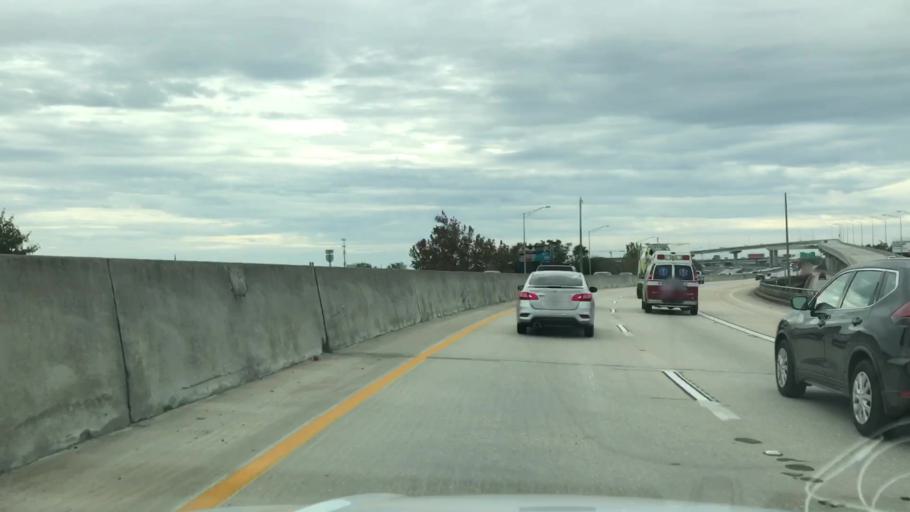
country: US
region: South Carolina
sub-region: Charleston County
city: Charleston
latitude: 32.8103
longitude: -79.9502
